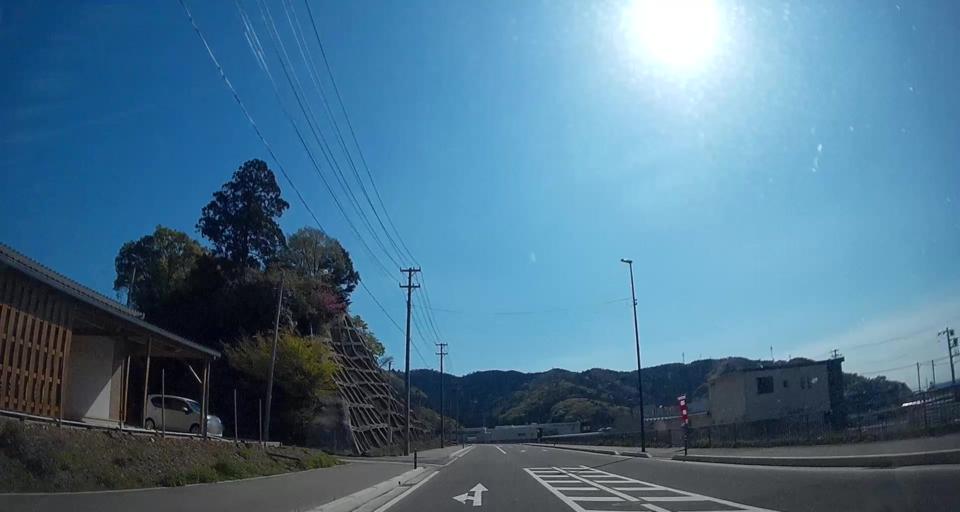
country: JP
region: Miyagi
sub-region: Oshika Gun
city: Onagawa Cho
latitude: 38.4461
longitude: 141.4530
